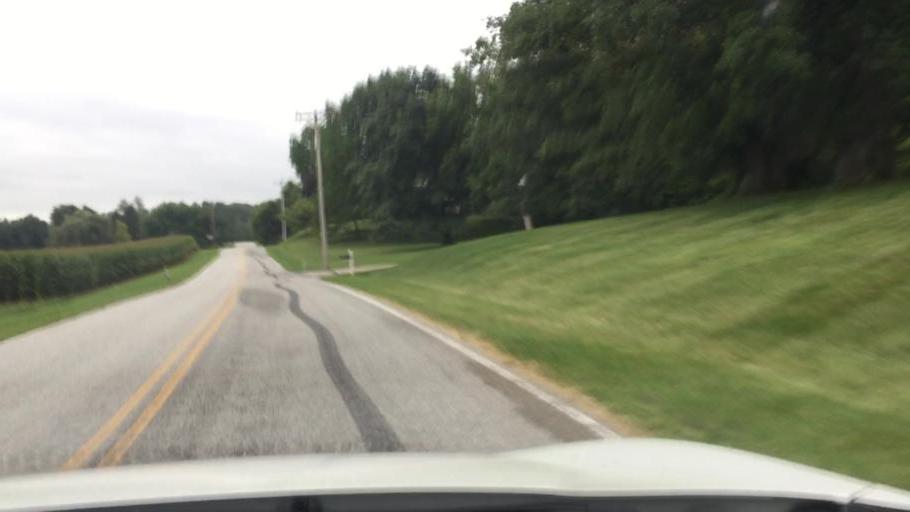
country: US
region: Ohio
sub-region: Champaign County
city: Mechanicsburg
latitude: 40.0642
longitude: -83.5891
